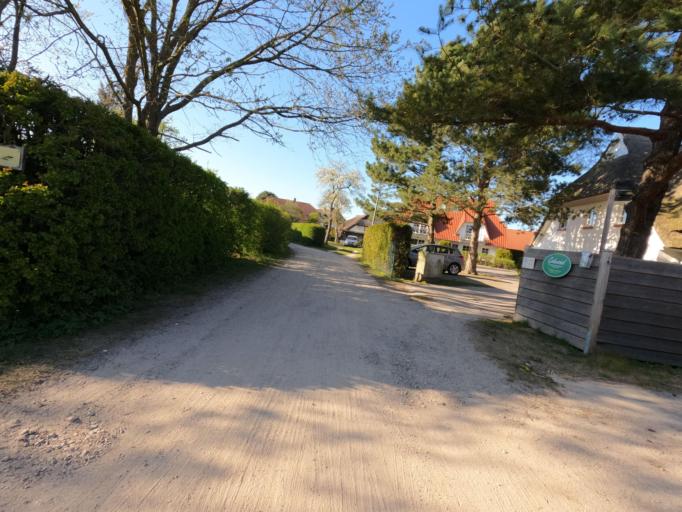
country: DE
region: Mecklenburg-Vorpommern
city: Born
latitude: 54.3901
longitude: 12.5392
